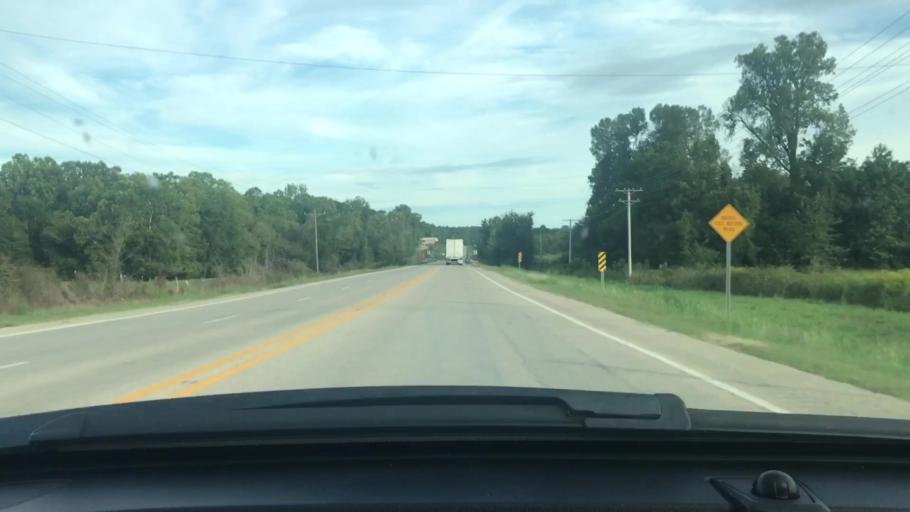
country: US
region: Arkansas
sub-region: Lawrence County
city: Hoxie
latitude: 36.1223
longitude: -91.1503
